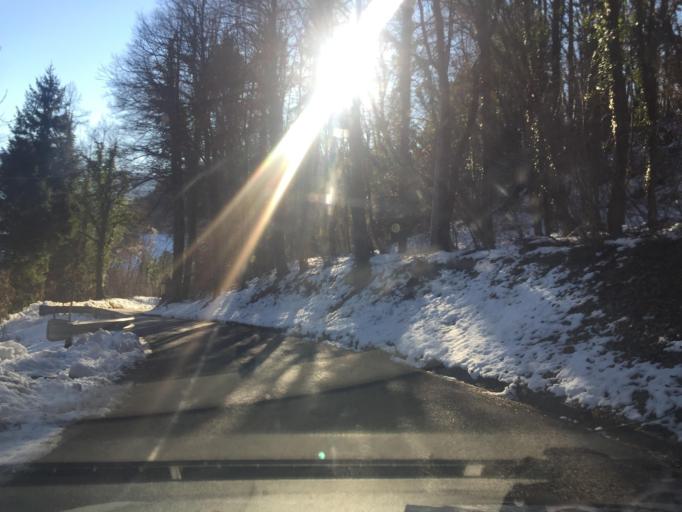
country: IT
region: Friuli Venezia Giulia
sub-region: Provincia di Udine
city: Tolmezzo
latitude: 46.4200
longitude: 12.9996
